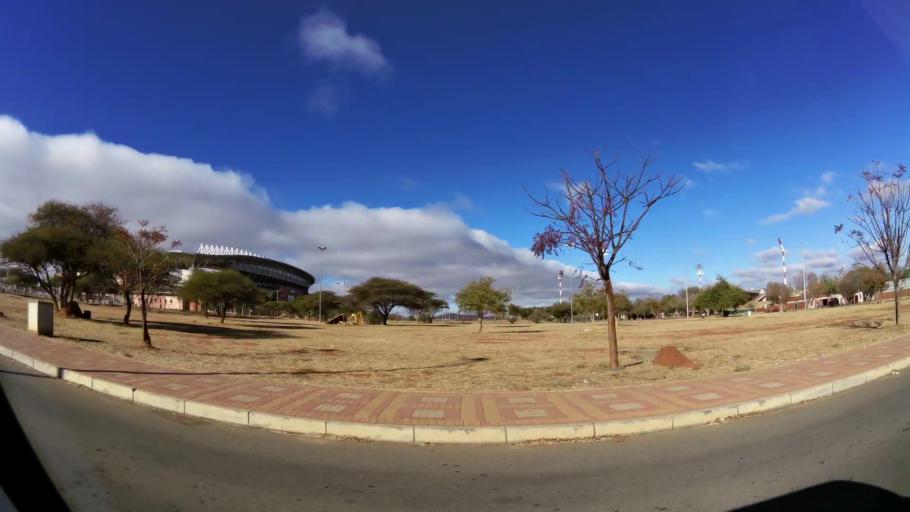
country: ZA
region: Limpopo
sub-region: Capricorn District Municipality
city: Polokwane
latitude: -23.9216
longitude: 29.4671
